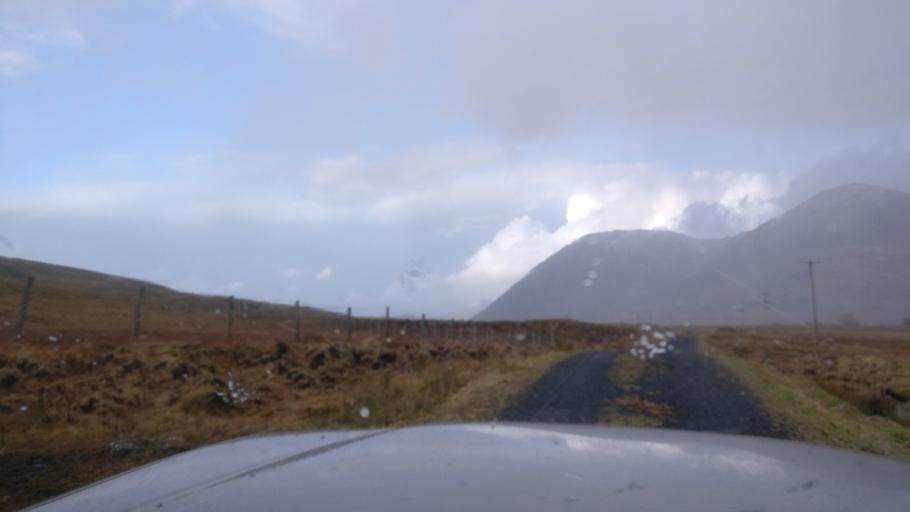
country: IE
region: Connaught
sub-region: County Galway
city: Clifden
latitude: 53.4930
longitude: -9.7031
